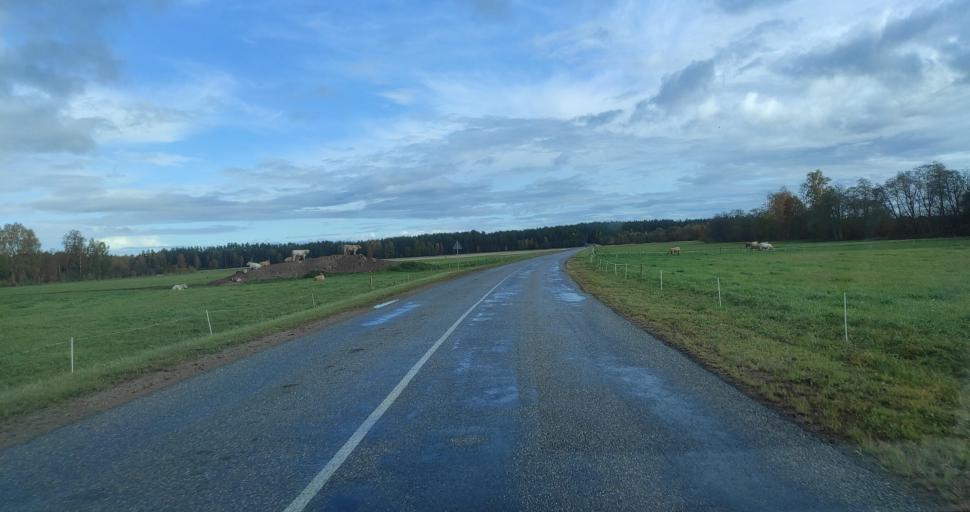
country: LV
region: Skrunda
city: Skrunda
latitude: 56.6272
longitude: 21.9860
